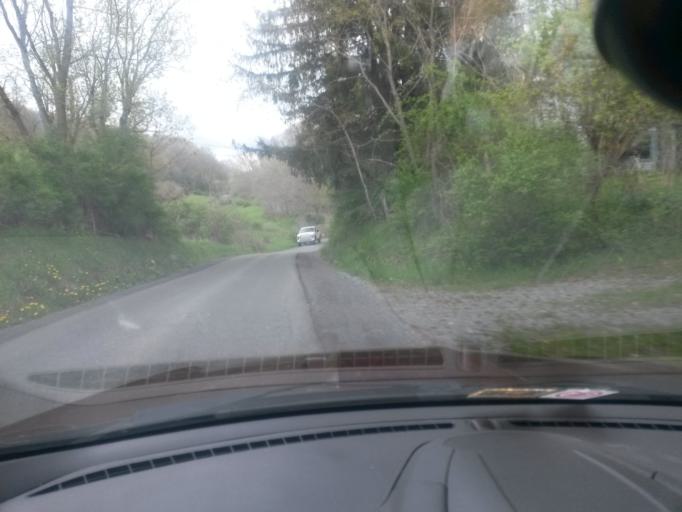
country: US
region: West Virginia
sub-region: Greenbrier County
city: Lewisburg
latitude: 37.9388
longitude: -80.4294
